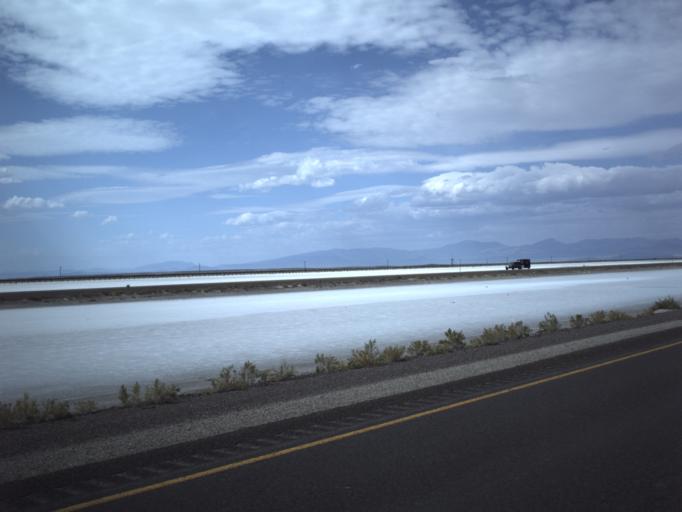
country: US
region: Utah
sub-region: Tooele County
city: Wendover
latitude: 40.7365
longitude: -113.7120
